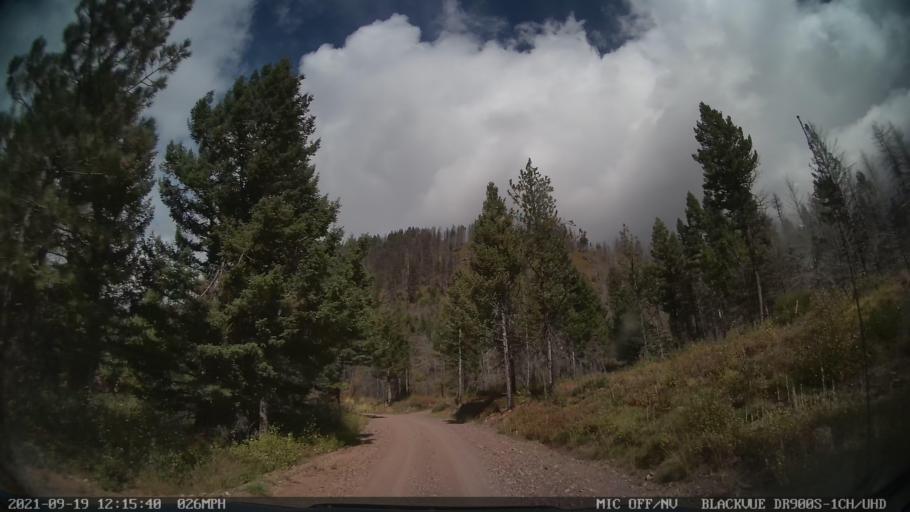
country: US
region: Montana
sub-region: Missoula County
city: Seeley Lake
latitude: 47.1676
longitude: -113.3455
